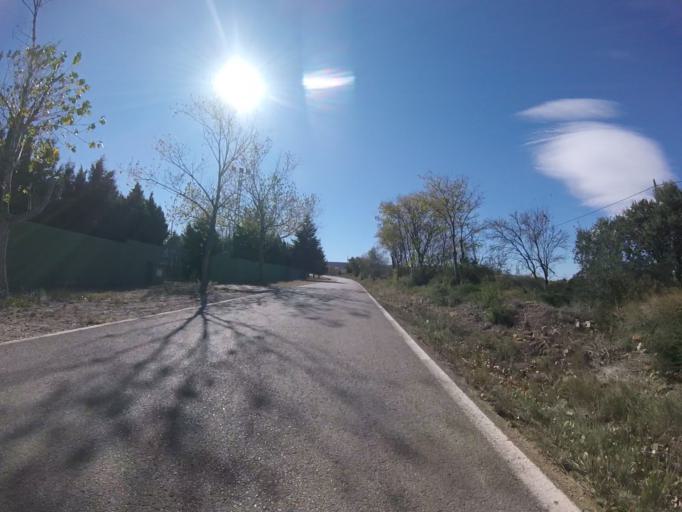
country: ES
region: Valencia
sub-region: Provincia de Castello
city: Albocasser
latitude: 40.3661
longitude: 0.0205
